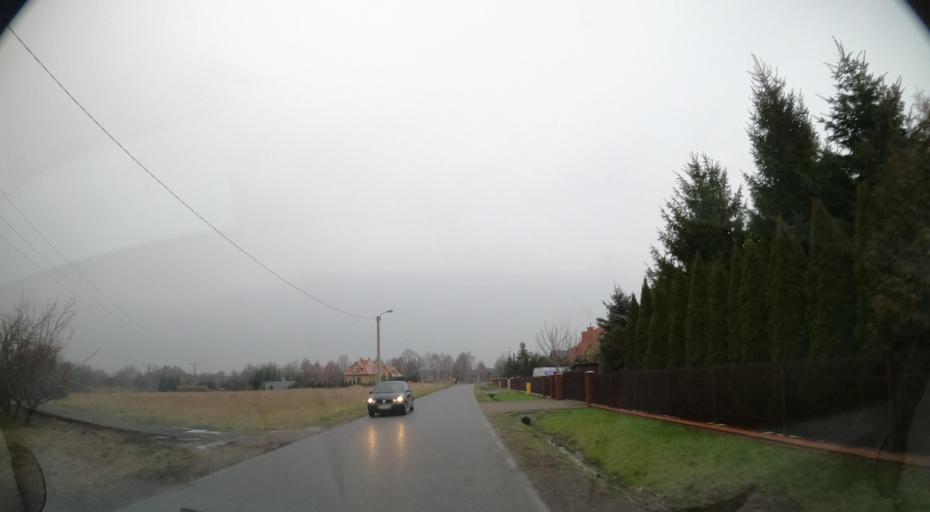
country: PL
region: Masovian Voivodeship
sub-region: Radom
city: Radom
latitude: 51.4179
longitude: 21.2238
